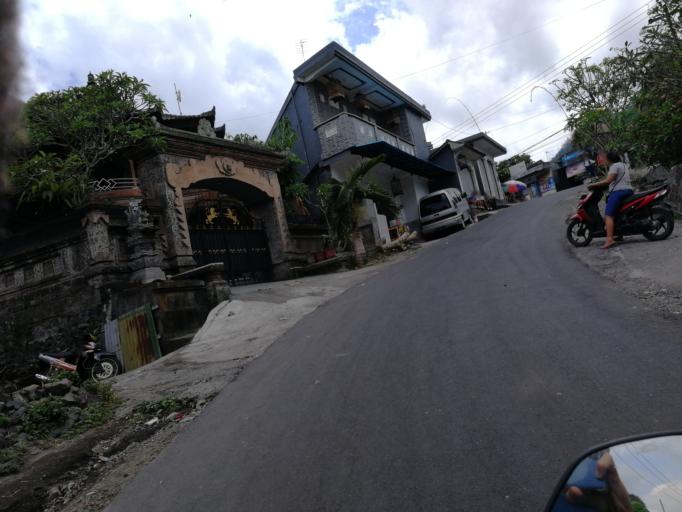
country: ID
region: Bali
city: Banjar Wangsian
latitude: -8.4650
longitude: 115.4474
